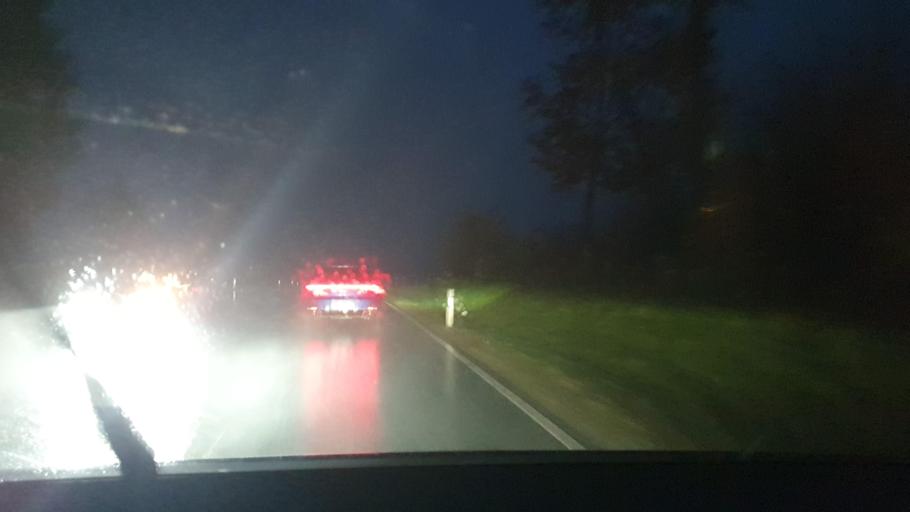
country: DE
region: Rheinland-Pfalz
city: Waldmuhlen
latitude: 50.5768
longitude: 8.0634
